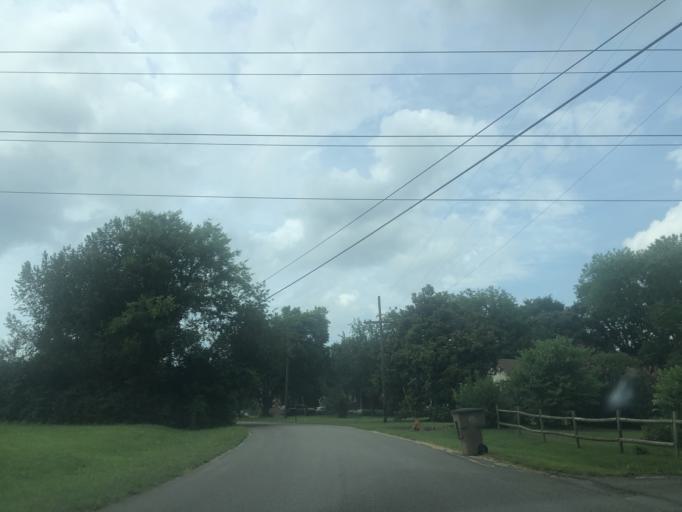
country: US
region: Tennessee
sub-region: Davidson County
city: Nashville
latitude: 36.1570
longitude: -86.6879
